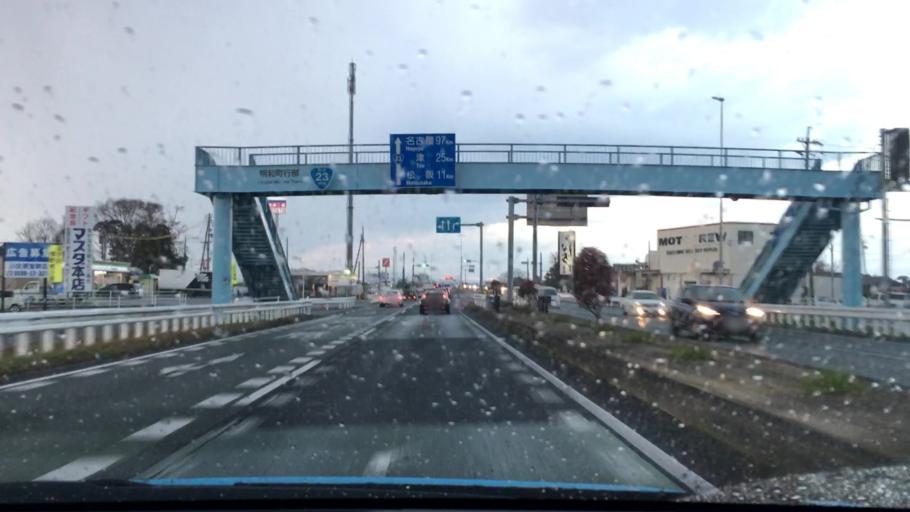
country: JP
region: Mie
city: Ise
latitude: 34.5720
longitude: 136.6296
